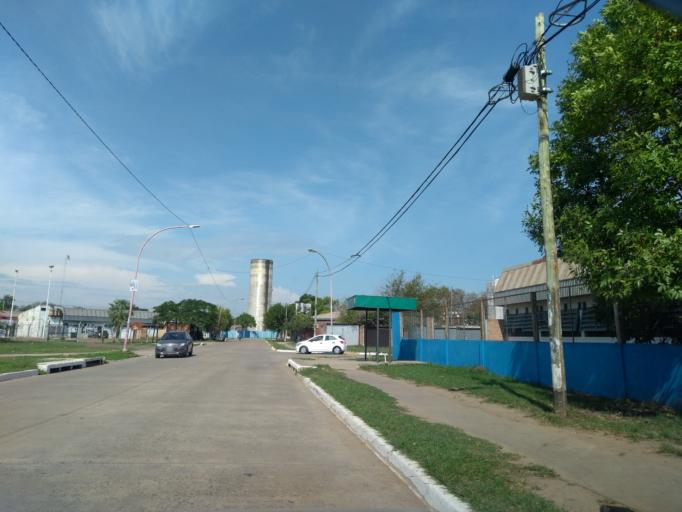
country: AR
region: Chaco
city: Barranqueras
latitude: -27.4624
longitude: -58.9489
